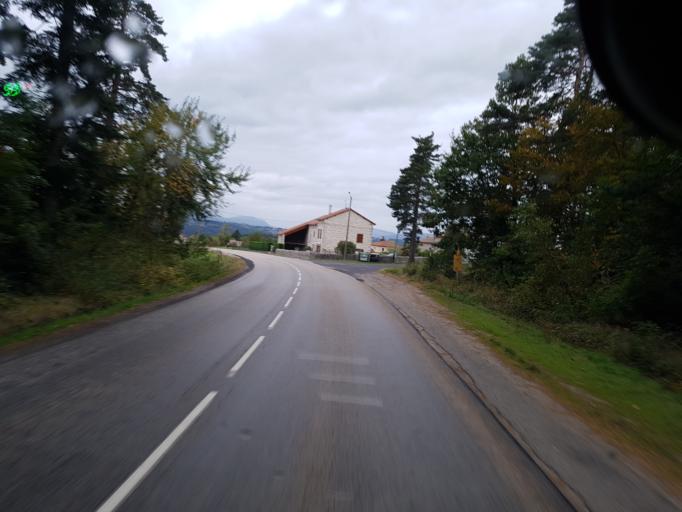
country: FR
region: Auvergne
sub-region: Departement de la Haute-Loire
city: Sainte-Sigolene
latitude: 45.2336
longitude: 4.2143
